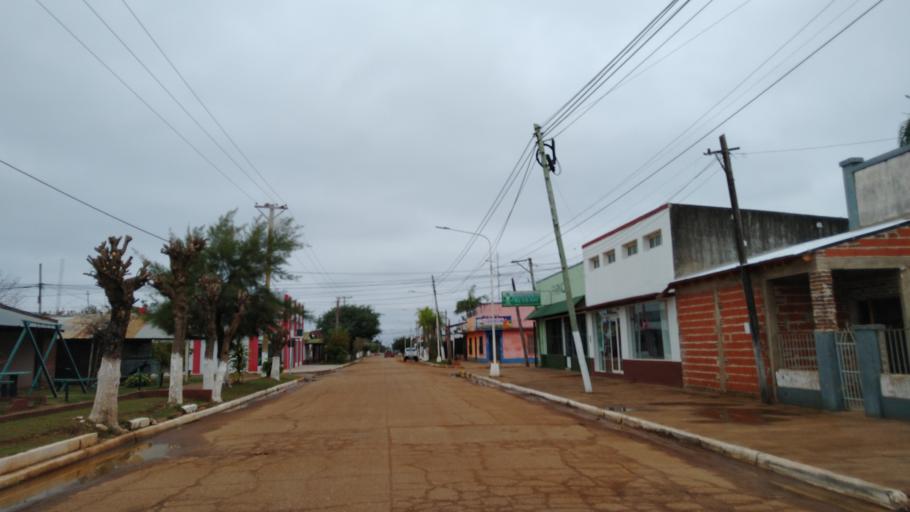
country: AR
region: Corrientes
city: Alvear
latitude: -29.0931
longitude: -56.5475
